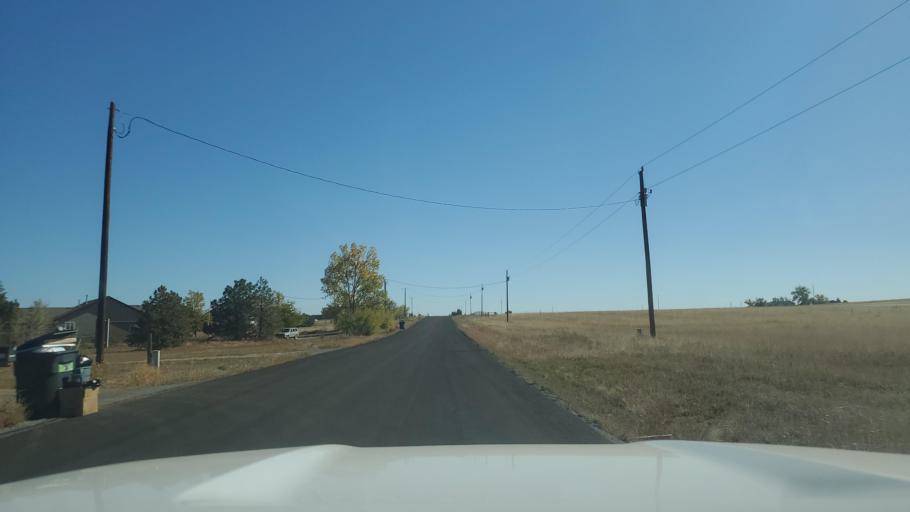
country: US
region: Colorado
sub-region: Adams County
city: Bennett
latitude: 39.7600
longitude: -104.3892
